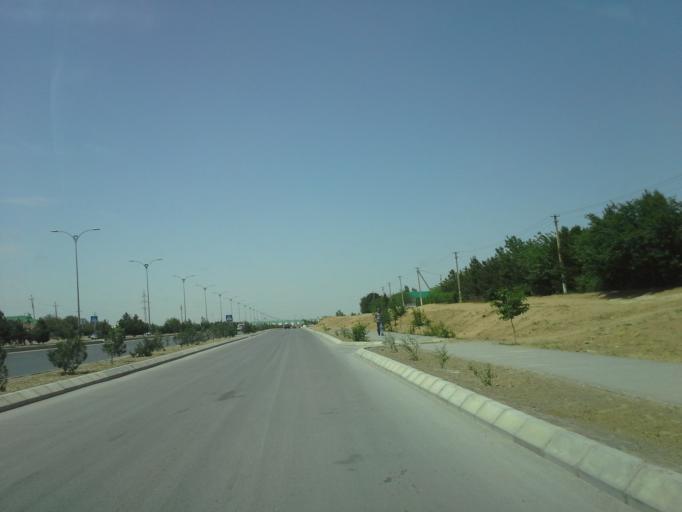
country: TM
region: Ahal
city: Ashgabat
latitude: 37.9999
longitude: 58.4070
